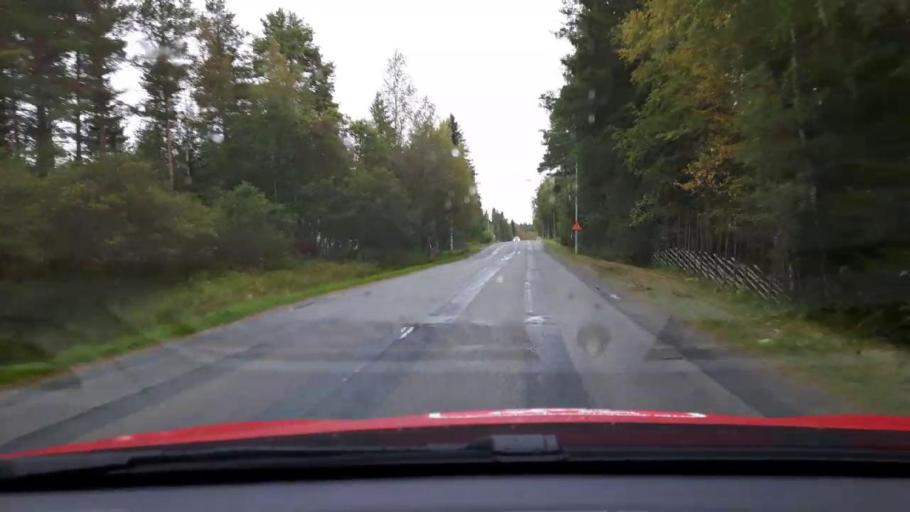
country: SE
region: Jaemtland
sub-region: Bergs Kommun
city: Hoverberg
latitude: 62.7758
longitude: 14.4302
